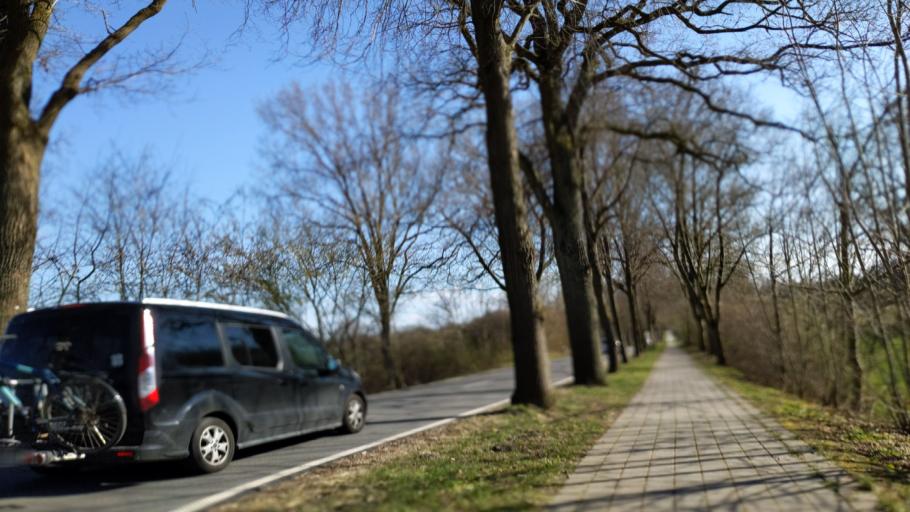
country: DE
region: Schleswig-Holstein
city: Eutin
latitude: 54.1020
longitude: 10.6124
